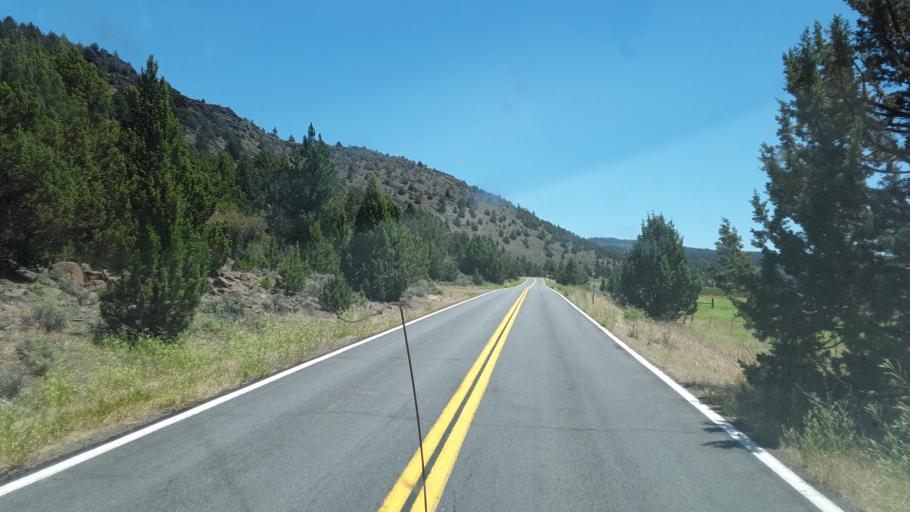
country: US
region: California
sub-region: Lassen County
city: Susanville
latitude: 40.6642
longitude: -120.6577
